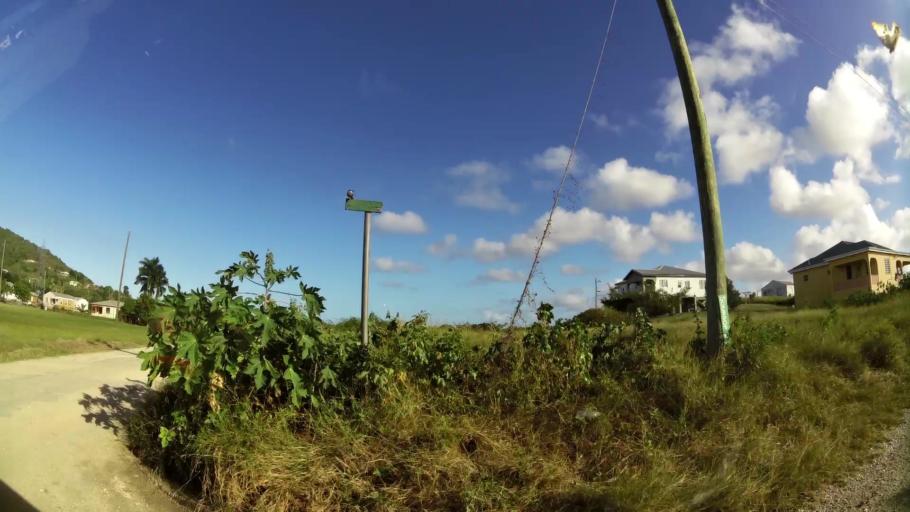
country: AG
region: Saint George
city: Piggotts
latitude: 17.1210
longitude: -61.8048
